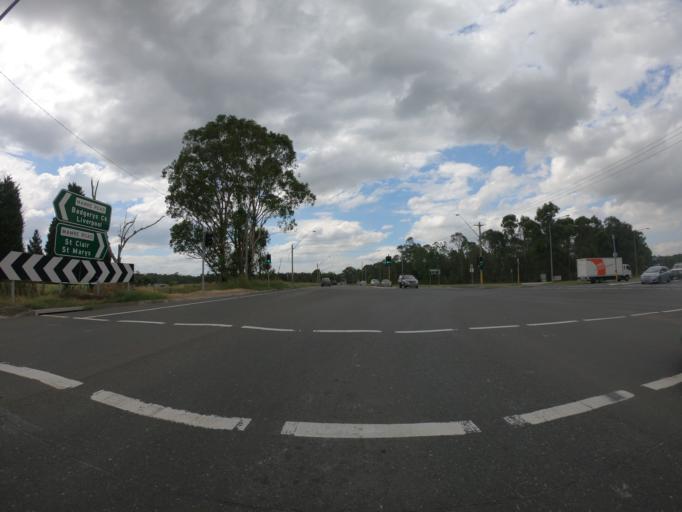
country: AU
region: New South Wales
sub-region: Blacktown
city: Mount Druitt
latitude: -33.8179
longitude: 150.7760
